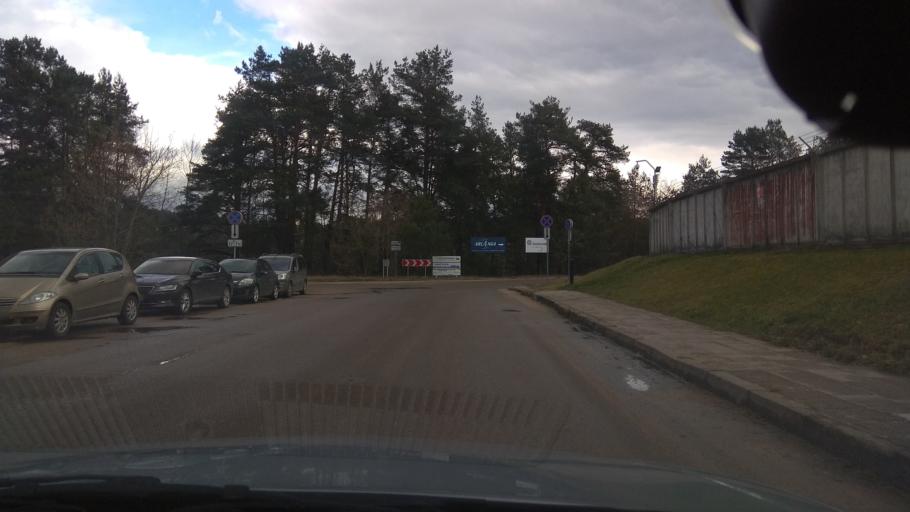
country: LT
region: Vilnius County
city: Lazdynai
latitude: 54.6534
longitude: 25.1891
